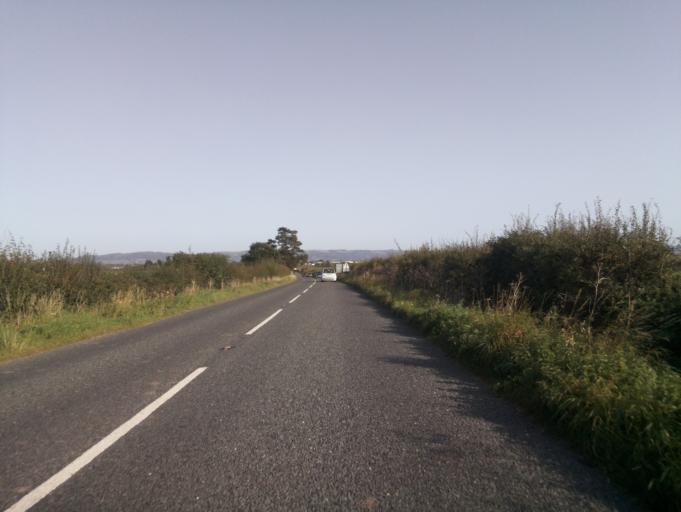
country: GB
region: England
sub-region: Gloucestershire
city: Tewkesbury
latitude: 51.9596
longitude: -2.1700
